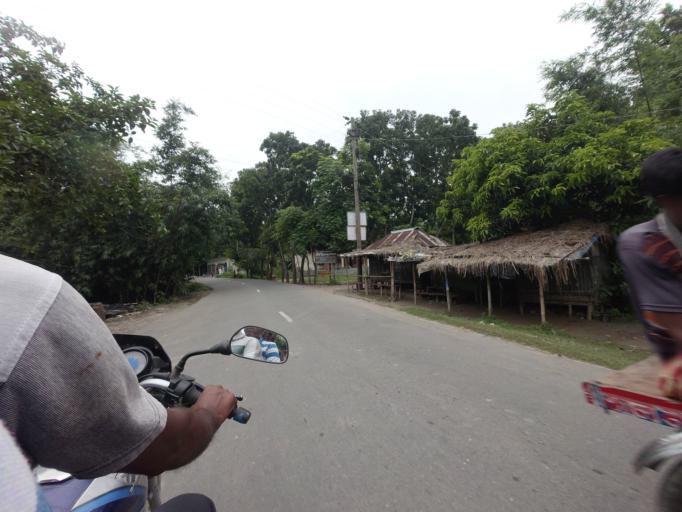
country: BD
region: Khulna
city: Kalia
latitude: 23.1674
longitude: 89.6455
